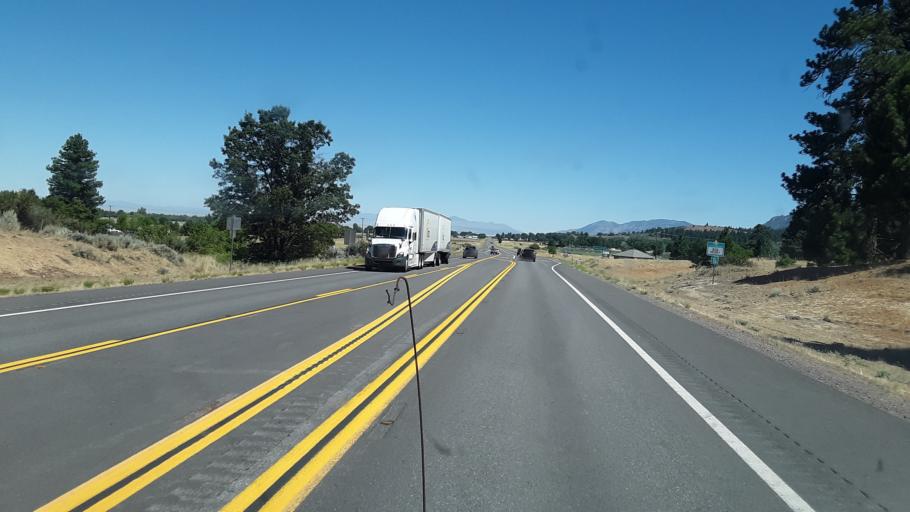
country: US
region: California
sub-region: Lassen County
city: Janesville
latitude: 40.3045
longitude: -120.5268
